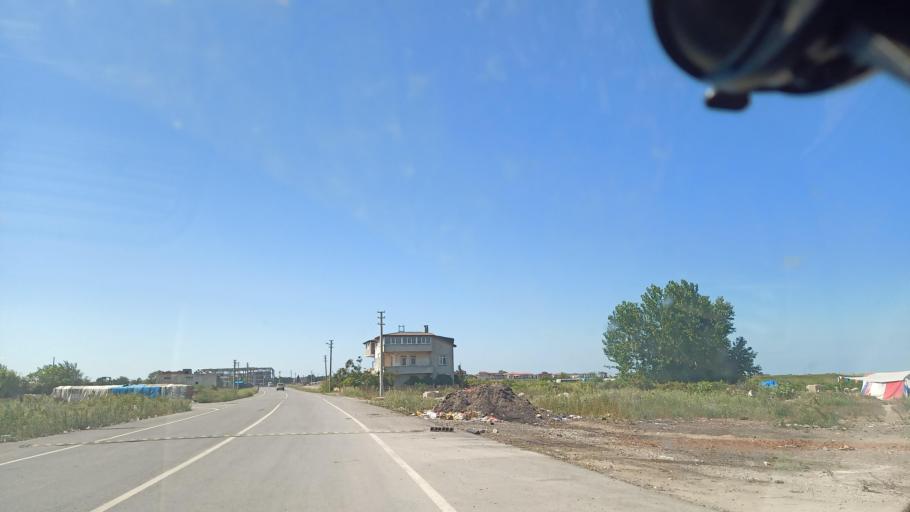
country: TR
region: Sakarya
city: Karasu
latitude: 41.1169
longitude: 30.6651
